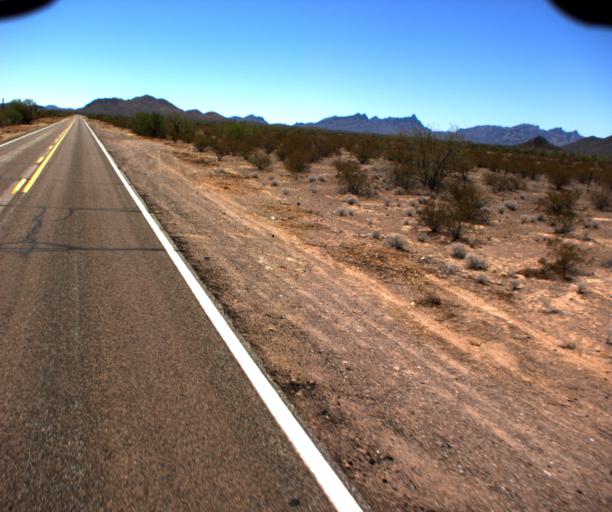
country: US
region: Arizona
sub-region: Pima County
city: Ajo
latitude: 32.2364
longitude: -112.7190
